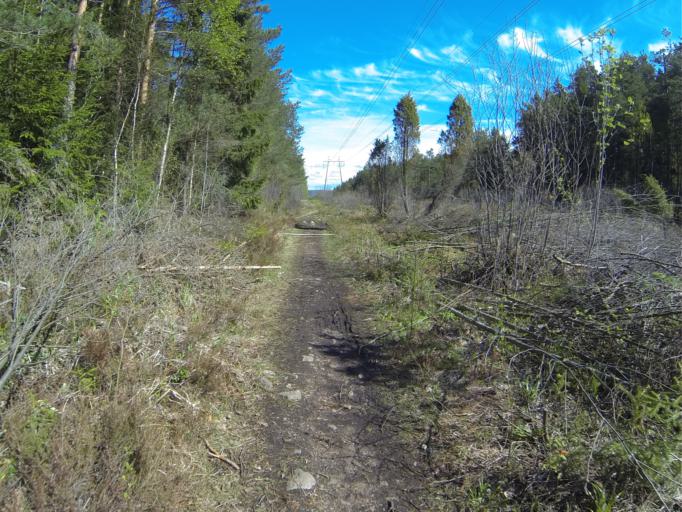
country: FI
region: Varsinais-Suomi
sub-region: Salo
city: Salo
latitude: 60.4016
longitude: 23.1954
